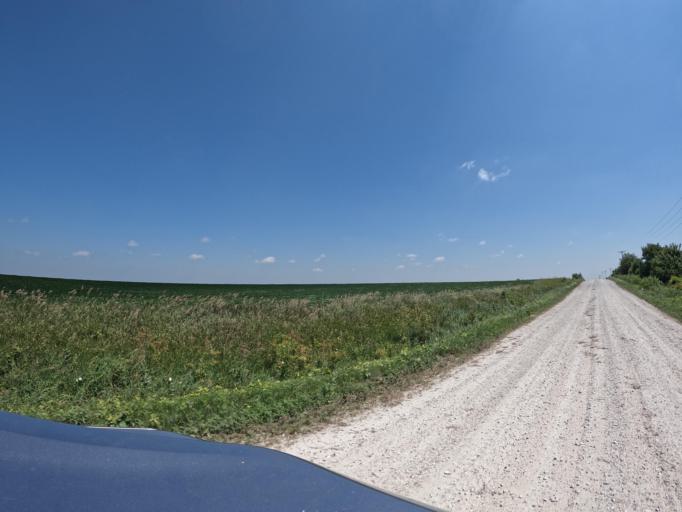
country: US
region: Iowa
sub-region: Keokuk County
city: Sigourney
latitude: 41.2794
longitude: -92.2308
